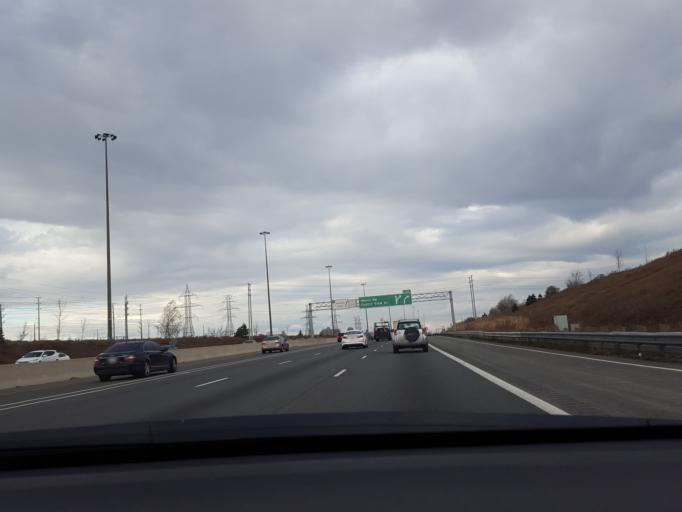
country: CA
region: Ontario
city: Mississauga
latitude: 43.5751
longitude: -79.6712
